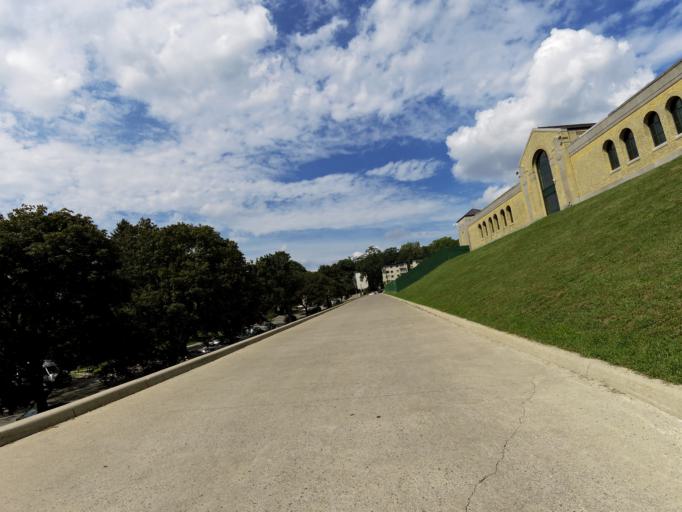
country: CA
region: Ontario
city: Scarborough
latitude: 43.6727
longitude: -79.2803
